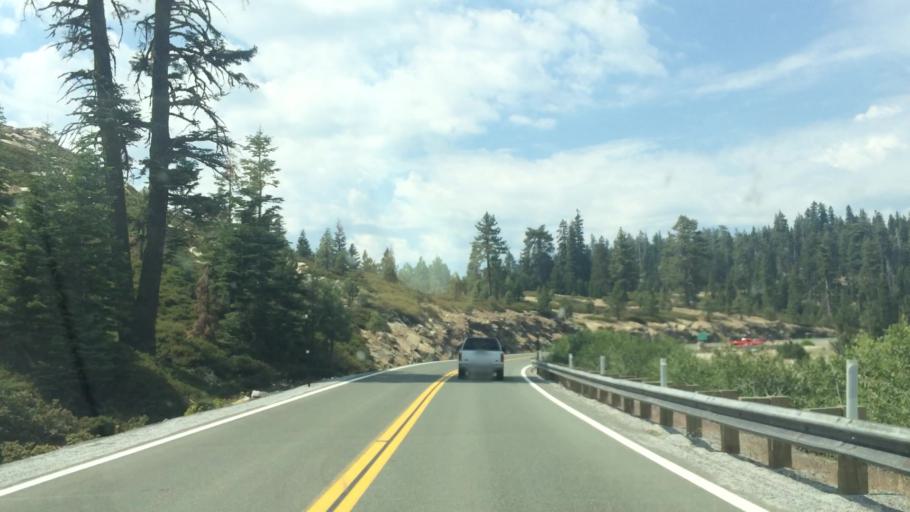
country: US
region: California
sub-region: Calaveras County
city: Arnold
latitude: 38.5632
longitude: -120.2658
